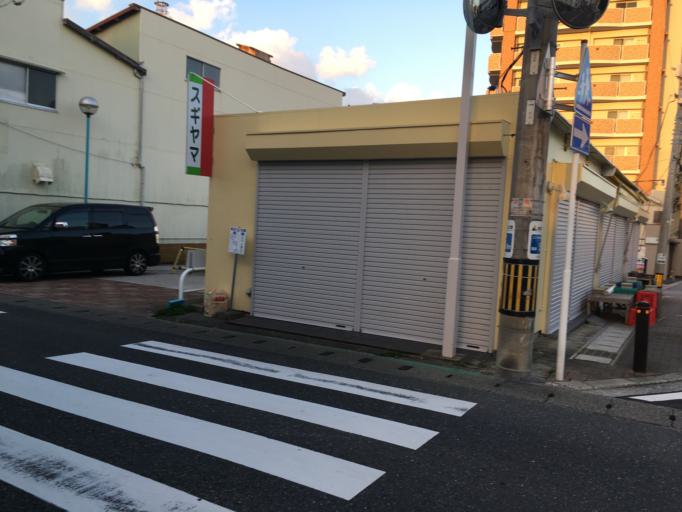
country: JP
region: Chiba
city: Tateyama
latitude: 34.9946
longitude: 139.8633
